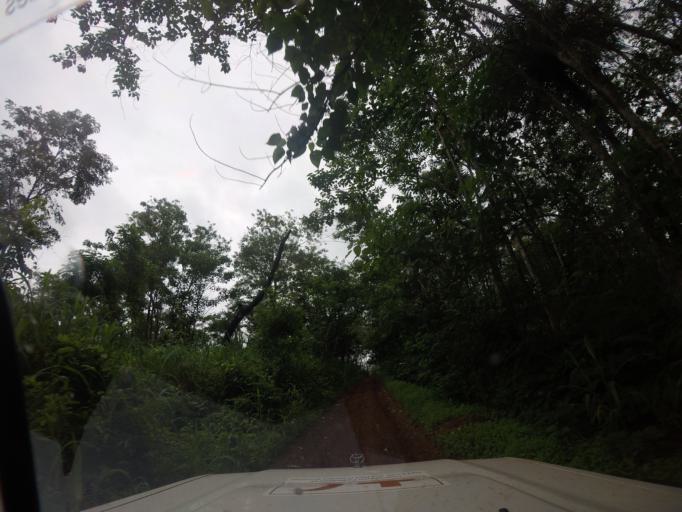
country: SL
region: Northern Province
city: Kamakwie
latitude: 9.6314
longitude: -12.2150
